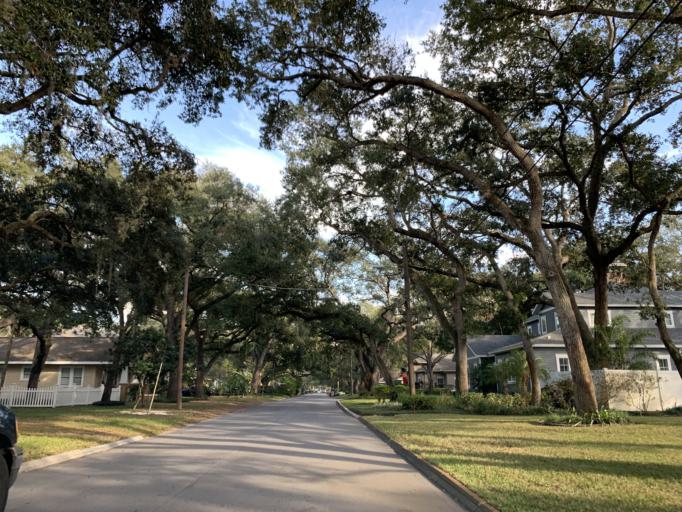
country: US
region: Florida
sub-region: Hillsborough County
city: Tampa
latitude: 27.9005
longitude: -82.4986
